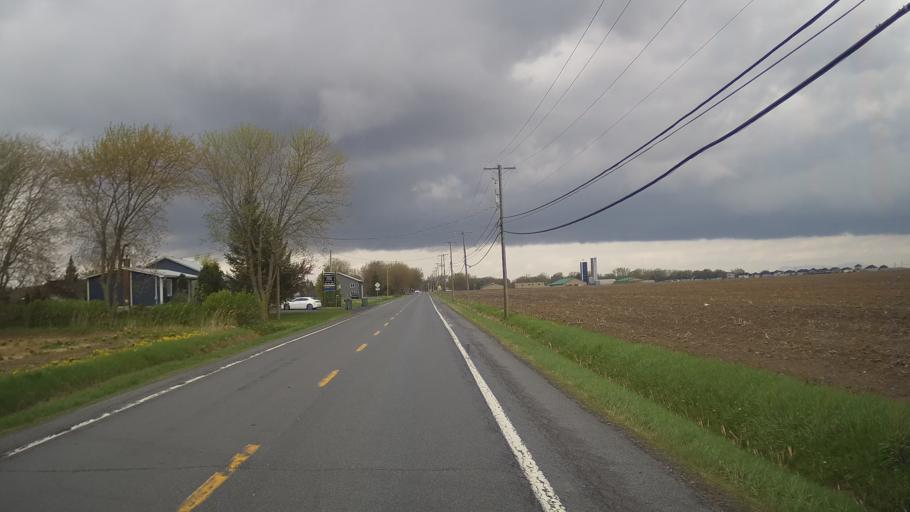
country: CA
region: Quebec
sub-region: Monteregie
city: Farnham
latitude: 45.3160
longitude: -73.0545
